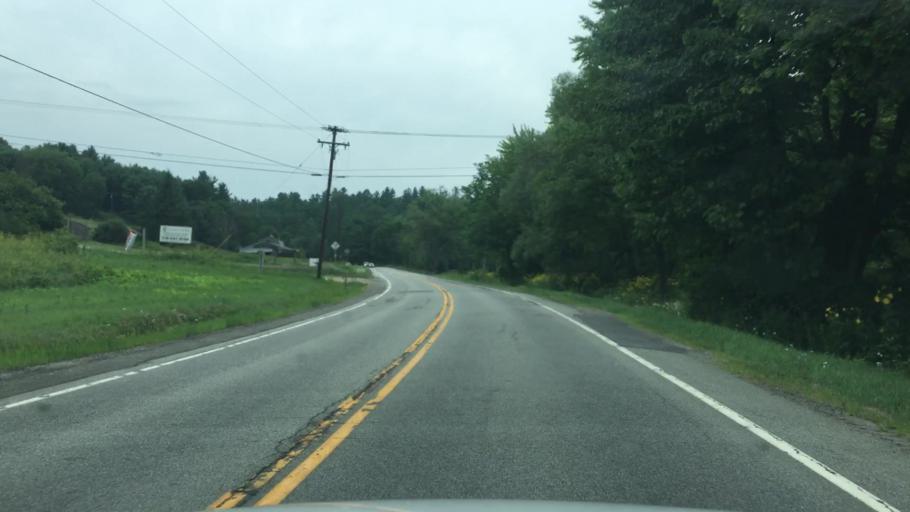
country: US
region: New York
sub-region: Essex County
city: Elizabethtown
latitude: 44.4142
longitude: -73.6807
